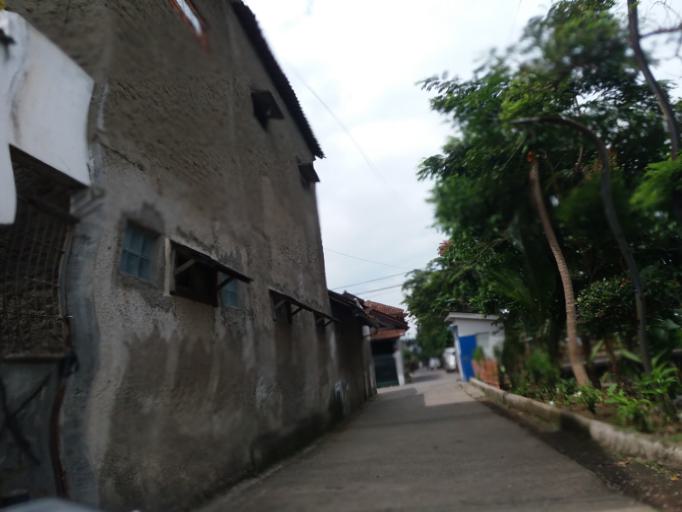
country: ID
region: West Java
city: Bandung
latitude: -6.9251
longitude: 107.6499
